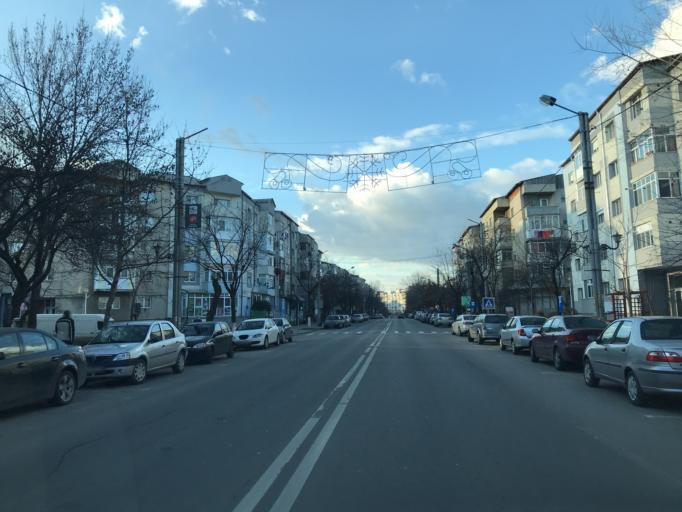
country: RO
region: Olt
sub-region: Municipiul Slatina
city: Slatina
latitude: 44.4238
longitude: 24.3803
